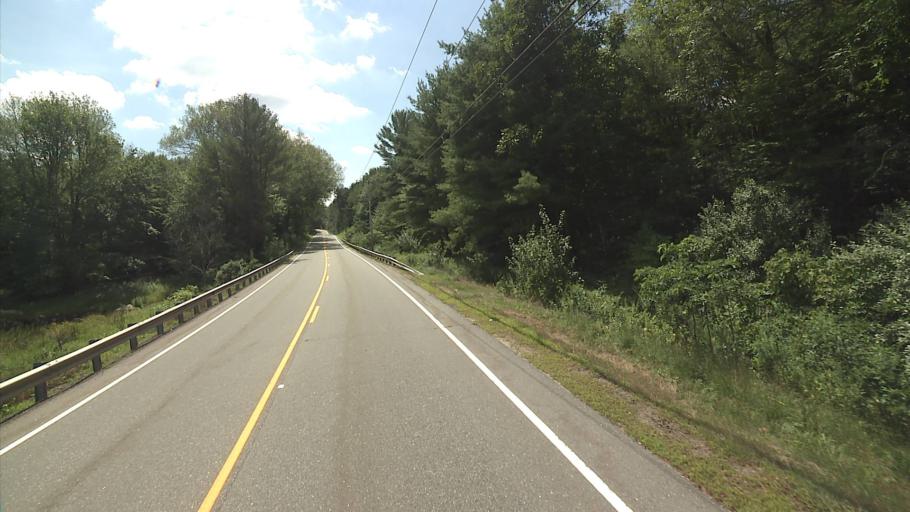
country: US
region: Massachusetts
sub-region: Worcester County
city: Southbridge
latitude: 41.9764
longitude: -72.0855
